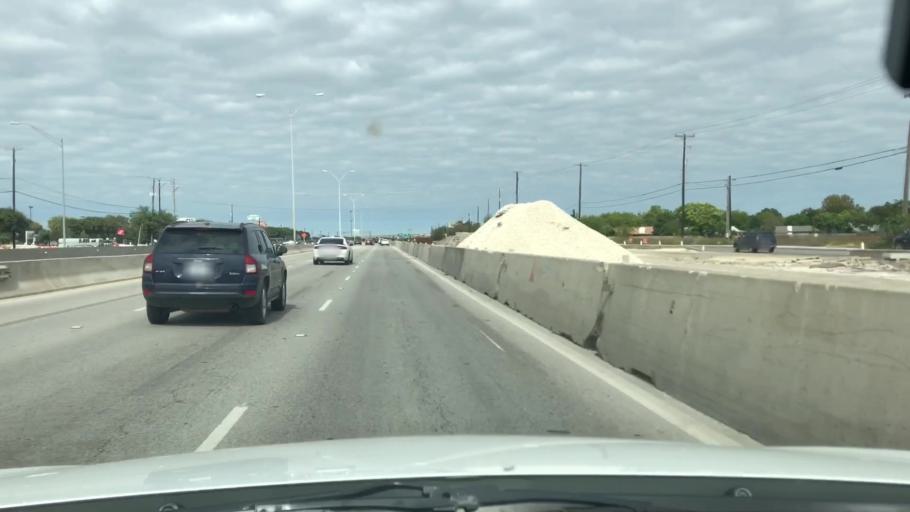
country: US
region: Texas
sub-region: Bexar County
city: Lackland Air Force Base
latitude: 29.4208
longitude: -98.6495
